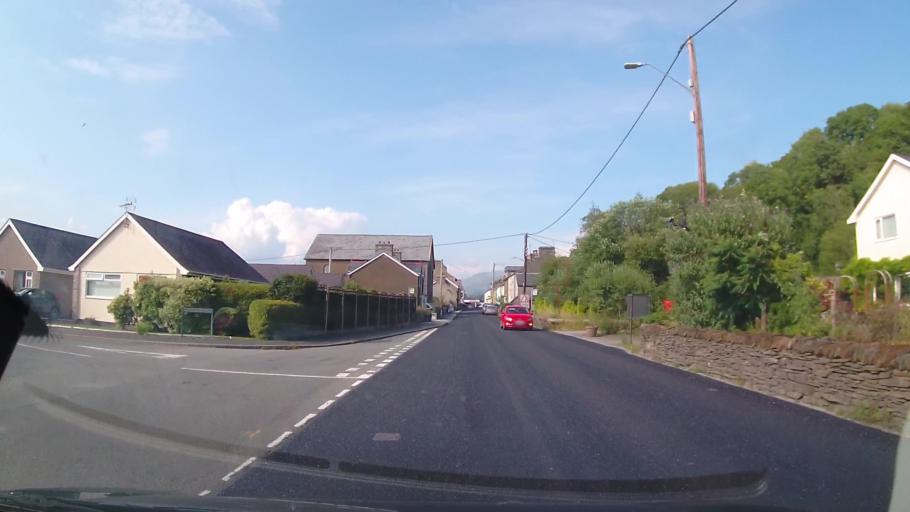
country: GB
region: Wales
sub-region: Gwynedd
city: Penrhyndeudraeth
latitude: 52.9021
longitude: -4.0657
